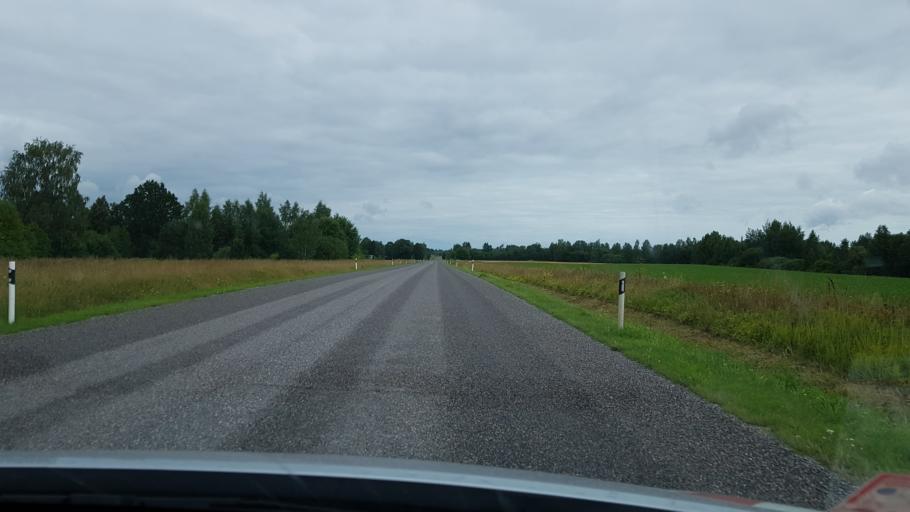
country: EE
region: Polvamaa
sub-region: Polva linn
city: Polva
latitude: 58.0059
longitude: 27.0600
